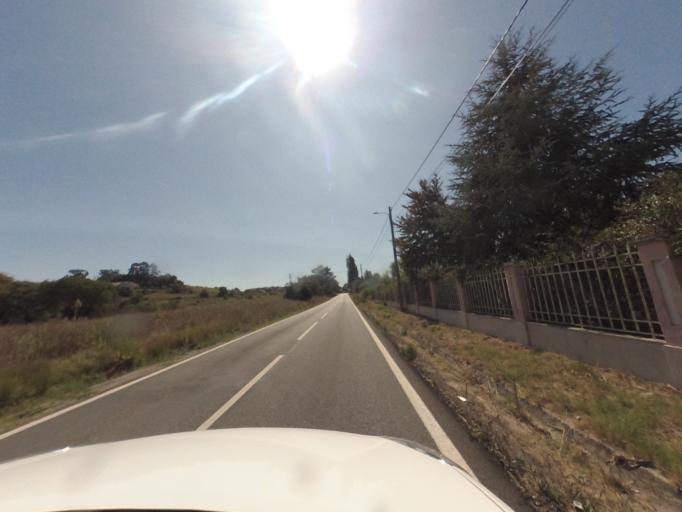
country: PT
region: Leiria
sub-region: Alcobaca
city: Alcobaca
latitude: 39.5247
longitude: -8.9668
